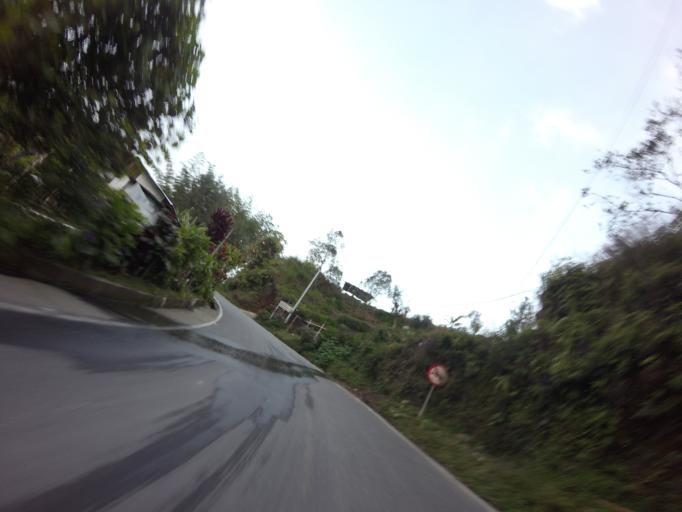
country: CO
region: Caldas
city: Manzanares
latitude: 5.3156
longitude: -75.1322
